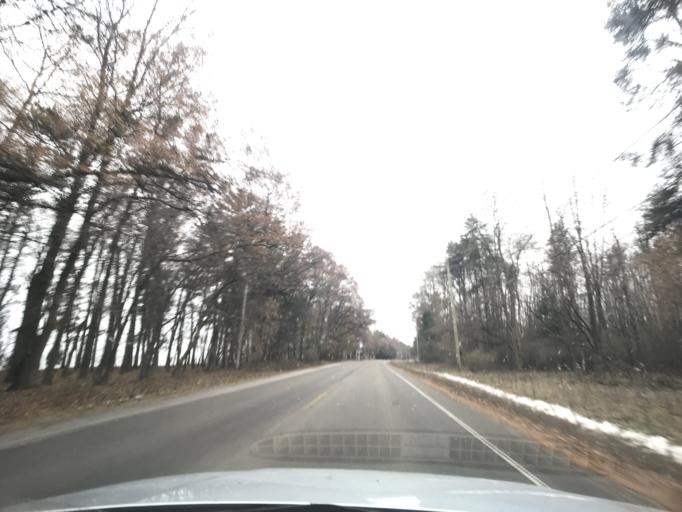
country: US
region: Wisconsin
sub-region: Marinette County
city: Marinette
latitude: 45.0590
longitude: -87.6205
